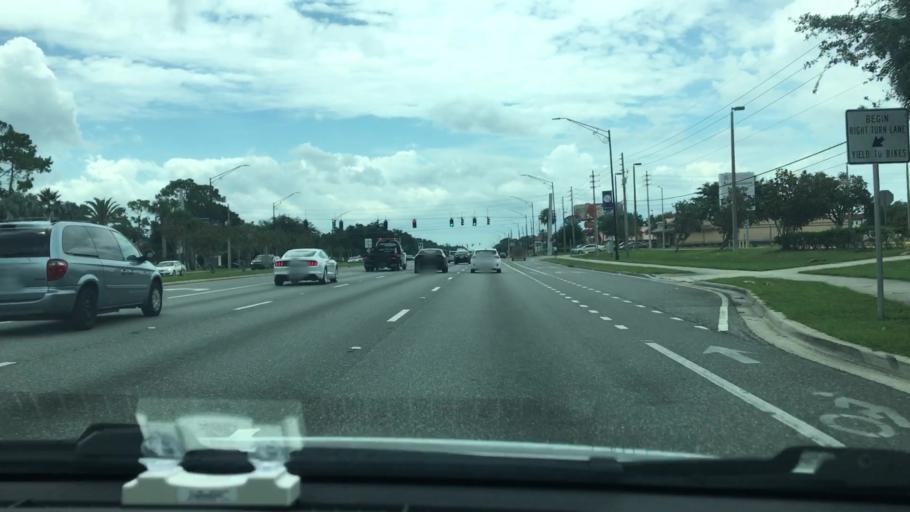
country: US
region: Florida
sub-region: Orange County
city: Azalea Park
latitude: 28.5183
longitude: -81.3105
